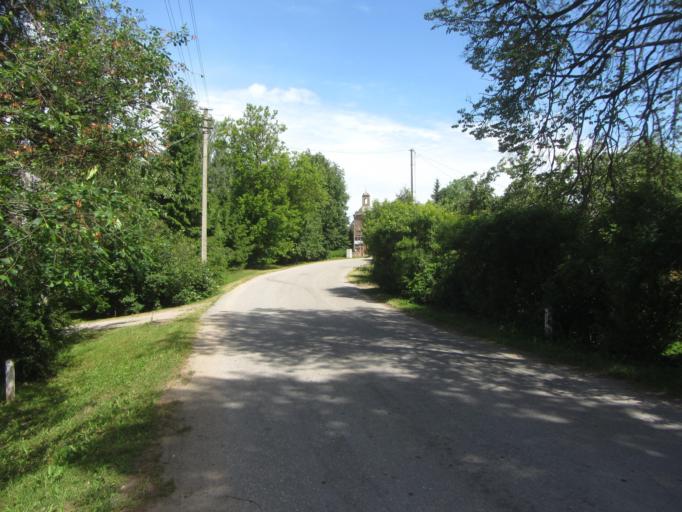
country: LV
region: Nereta
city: Nereta
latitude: 56.1479
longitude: 25.1388
